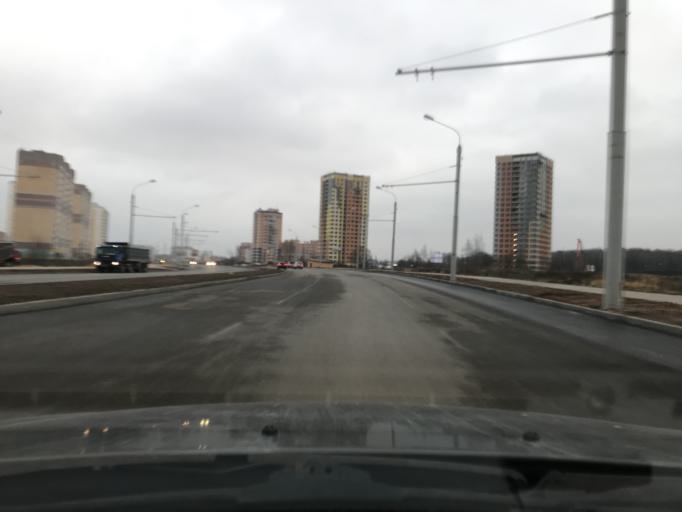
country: RU
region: Kaluga
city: Kaluga
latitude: 54.4888
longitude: 36.1956
